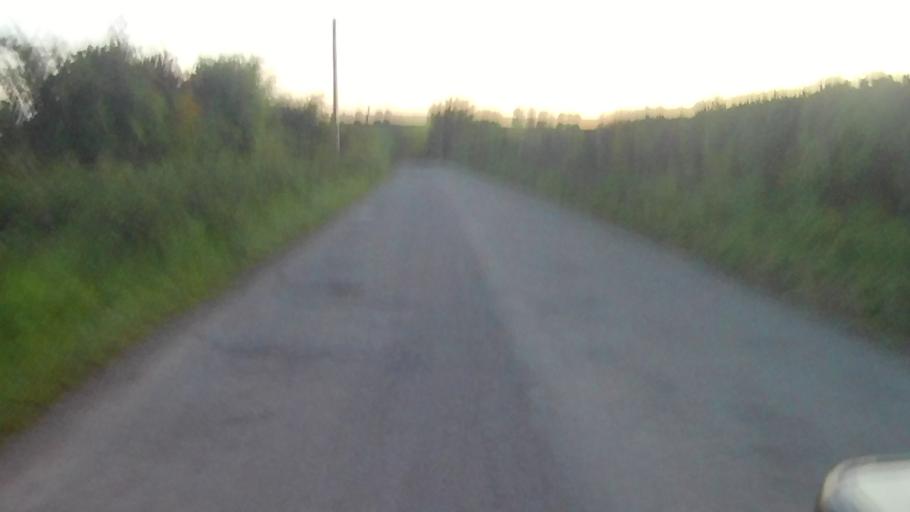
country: IE
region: Munster
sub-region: County Cork
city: Carrigtwohill
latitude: 51.9648
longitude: -8.2864
